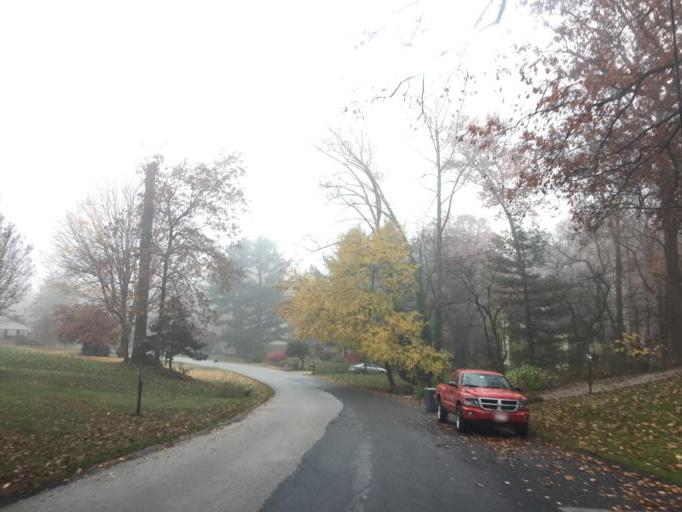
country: US
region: Maryland
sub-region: Howard County
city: Riverside
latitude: 39.1885
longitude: -76.8604
